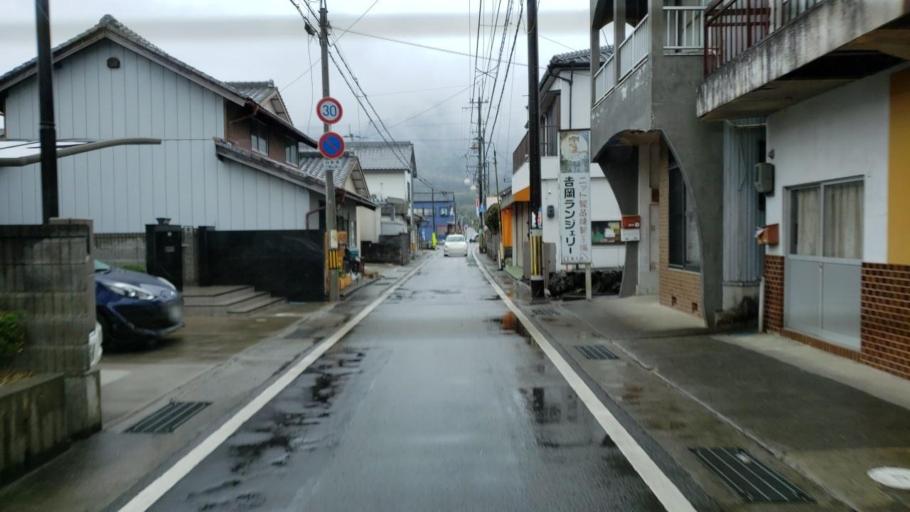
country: JP
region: Tokushima
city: Kamojimacho-jogejima
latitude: 34.0628
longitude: 134.3195
